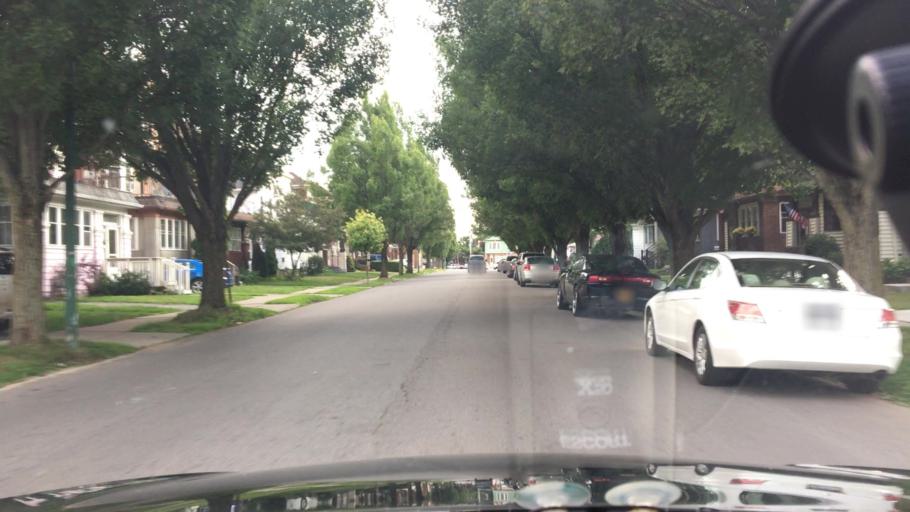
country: US
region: New York
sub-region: Erie County
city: West Seneca
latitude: 42.8551
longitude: -78.8184
